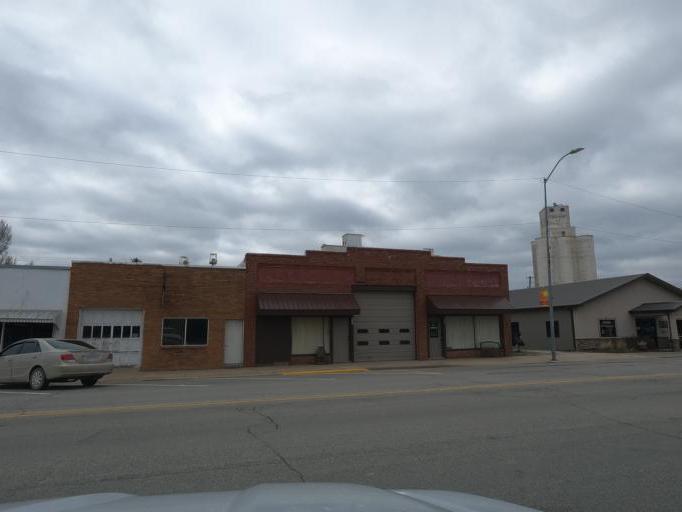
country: US
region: Kansas
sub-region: McPherson County
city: Inman
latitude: 38.2305
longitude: -97.7757
